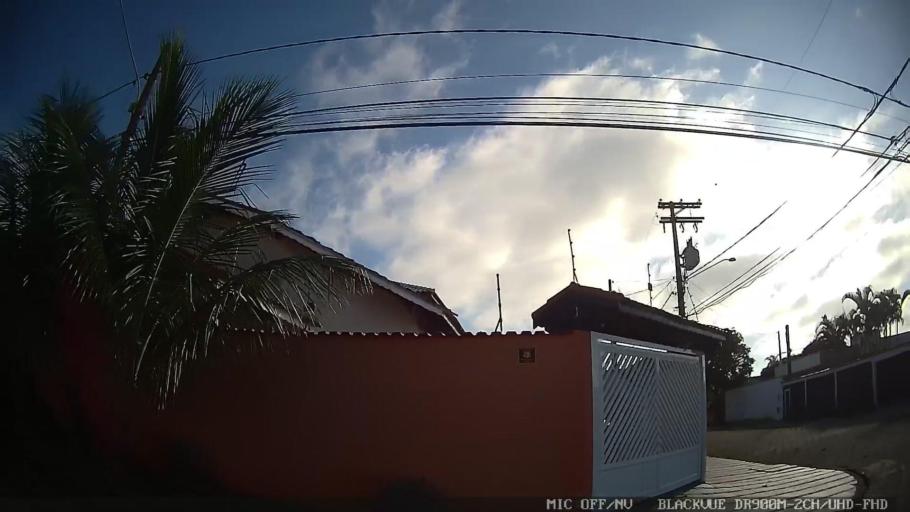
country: BR
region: Sao Paulo
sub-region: Peruibe
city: Peruibe
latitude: -24.3011
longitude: -46.9786
